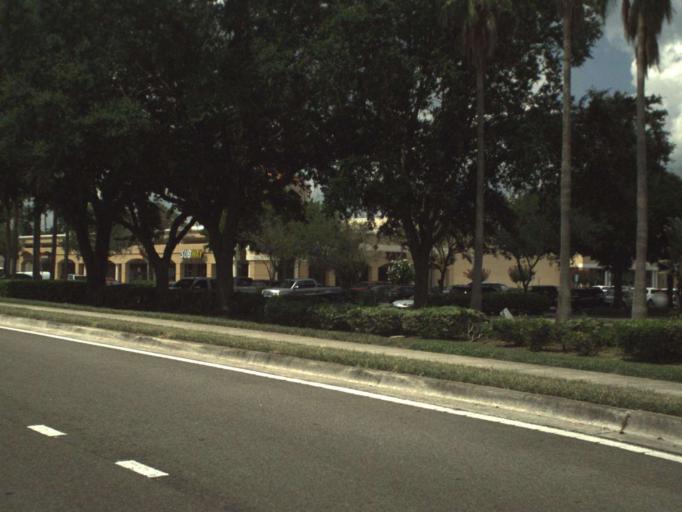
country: US
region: Florida
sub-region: Seminole County
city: Forest City
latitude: 28.6578
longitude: -81.4196
